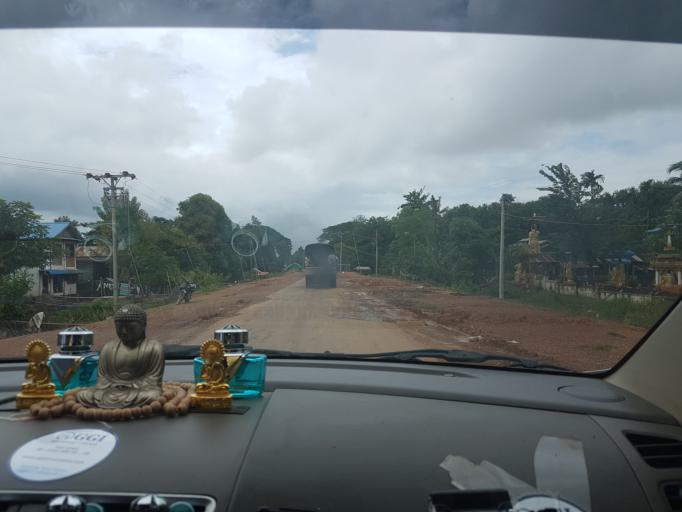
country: MM
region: Bago
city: Nyaunglebin
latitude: 17.9150
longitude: 96.8334
